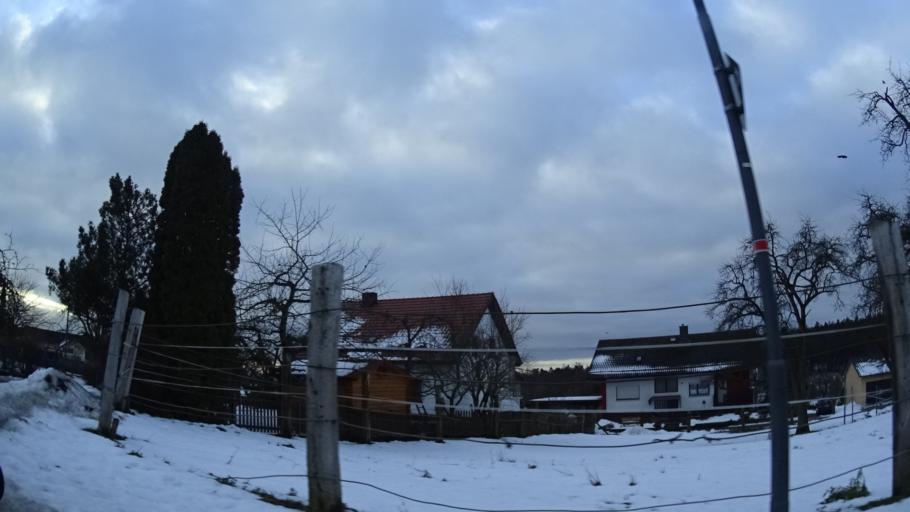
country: DE
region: Baden-Wuerttemberg
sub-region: Karlsruhe Region
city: Fahrenbach
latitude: 49.4730
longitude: 9.1555
